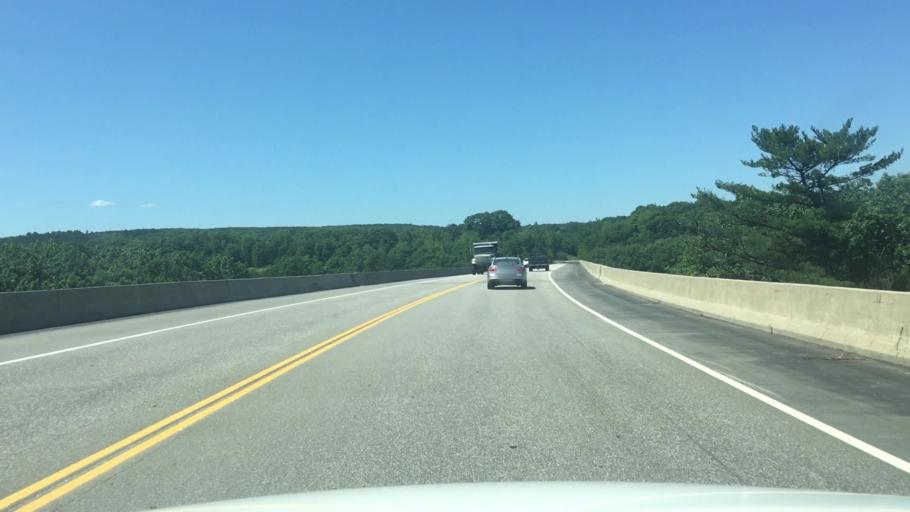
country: US
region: Maine
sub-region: Kennebec County
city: Waterville
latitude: 44.5292
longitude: -69.6446
